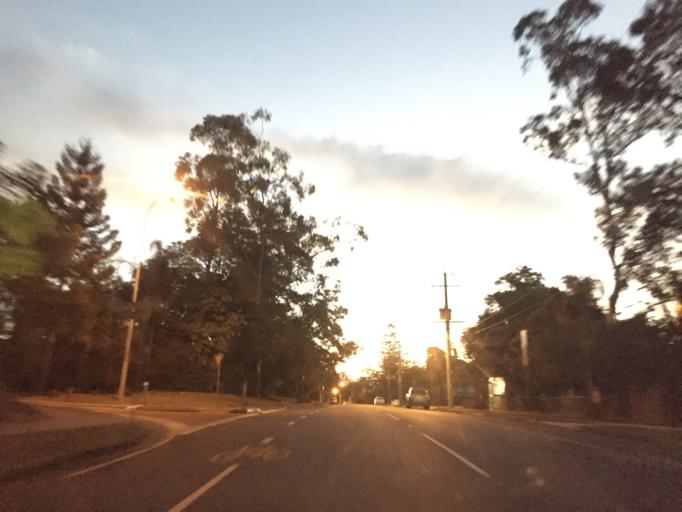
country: AU
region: Queensland
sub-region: Brisbane
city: Taringa
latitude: -27.4494
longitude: 152.9521
